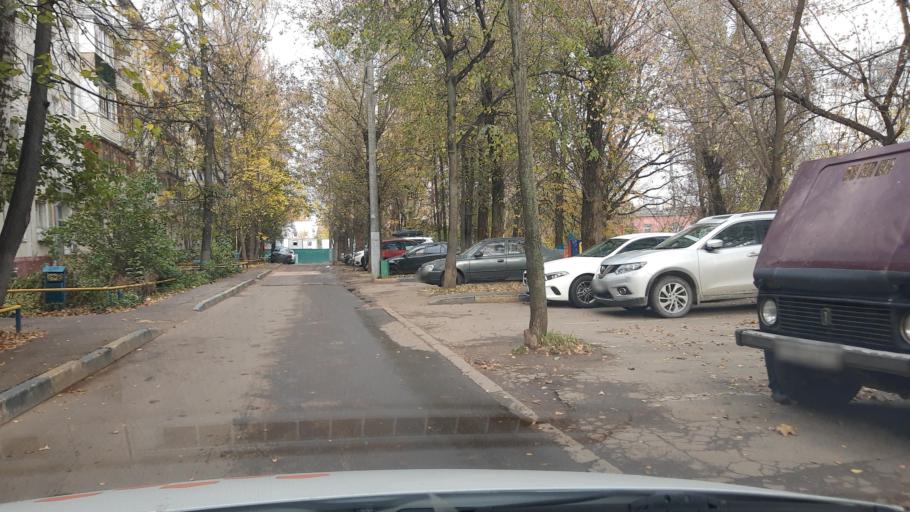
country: RU
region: Moscow
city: Zyuzino
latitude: 55.6532
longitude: 37.5759
